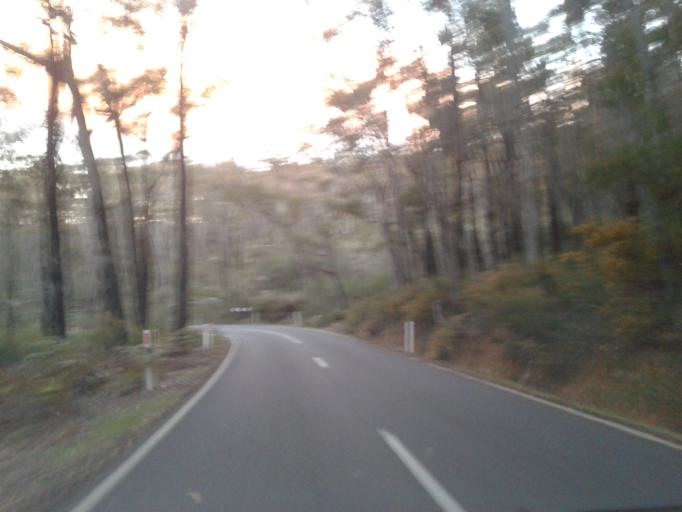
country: AU
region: Victoria
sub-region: Northern Grampians
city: Stawell
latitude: -37.1545
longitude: 142.4866
